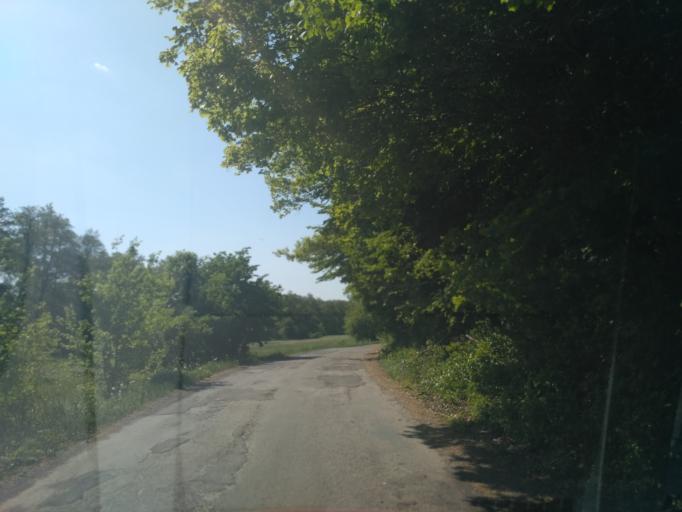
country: SK
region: Kosicky
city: Kosice
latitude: 48.8591
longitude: 21.4232
